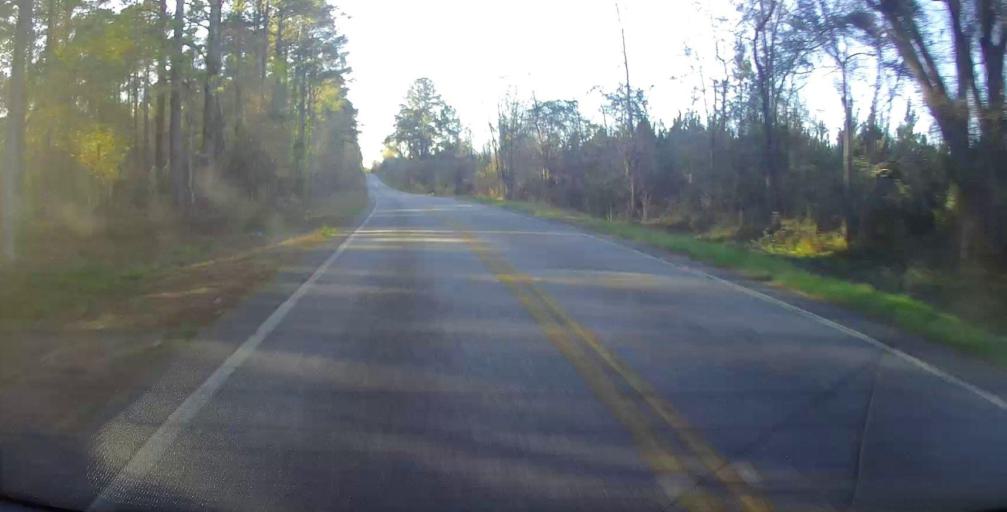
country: US
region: Georgia
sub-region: Wilcox County
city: Abbeville
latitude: 32.1029
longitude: -83.3062
